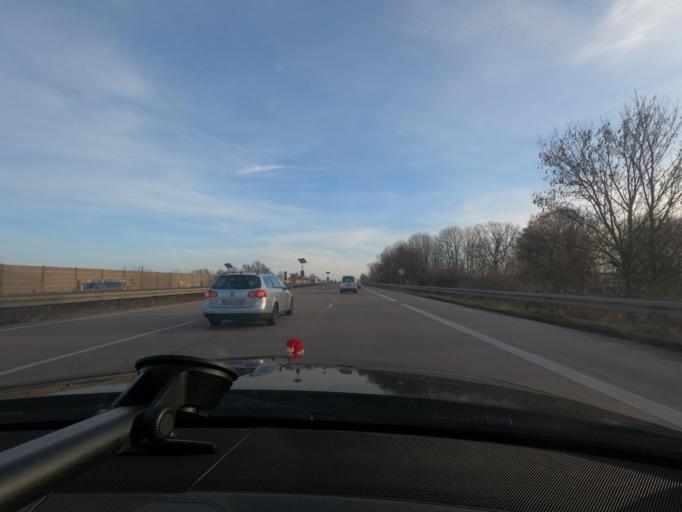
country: DE
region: Lower Saxony
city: Harsum
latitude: 52.1899
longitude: 9.9582
